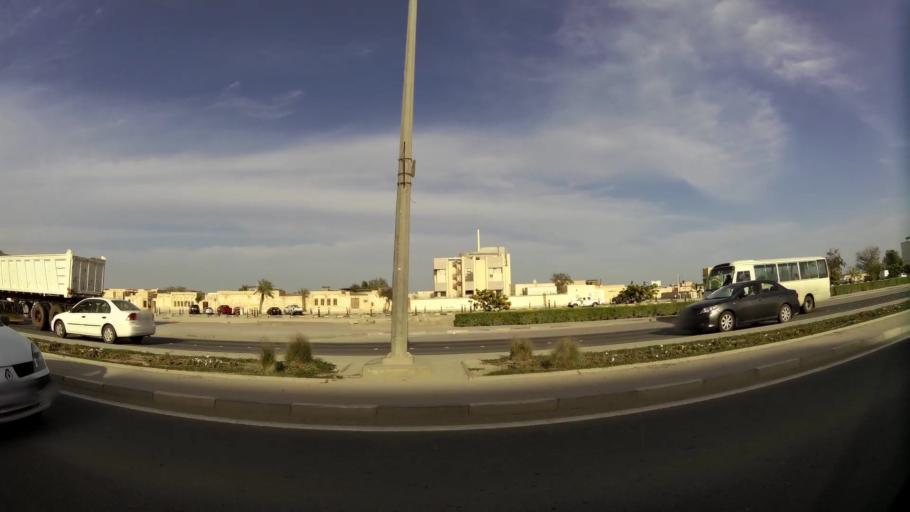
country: QA
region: Al Wakrah
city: Al Wakrah
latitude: 25.1683
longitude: 51.6075
